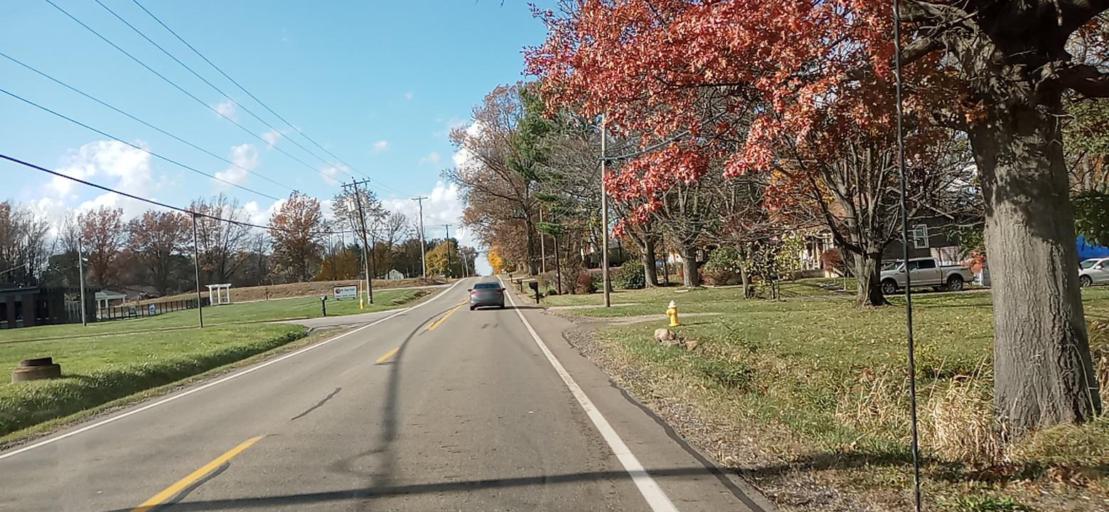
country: US
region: Ohio
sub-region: Summit County
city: Portage Lakes
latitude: 40.9976
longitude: -81.4992
